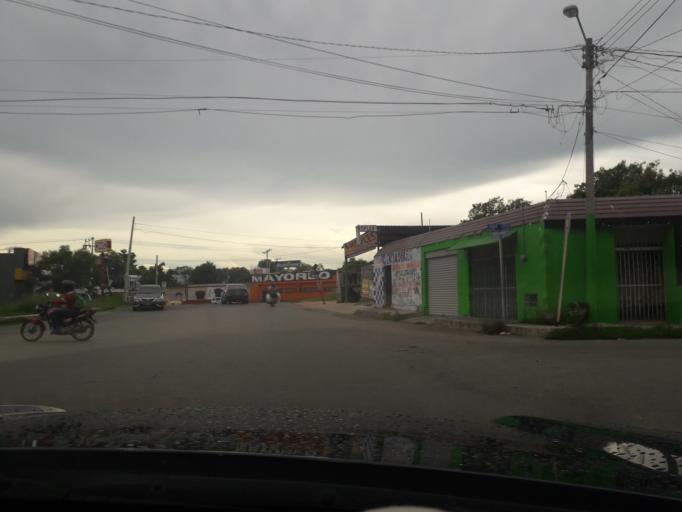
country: MX
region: Yucatan
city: Merida
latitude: 20.9600
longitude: -89.6473
